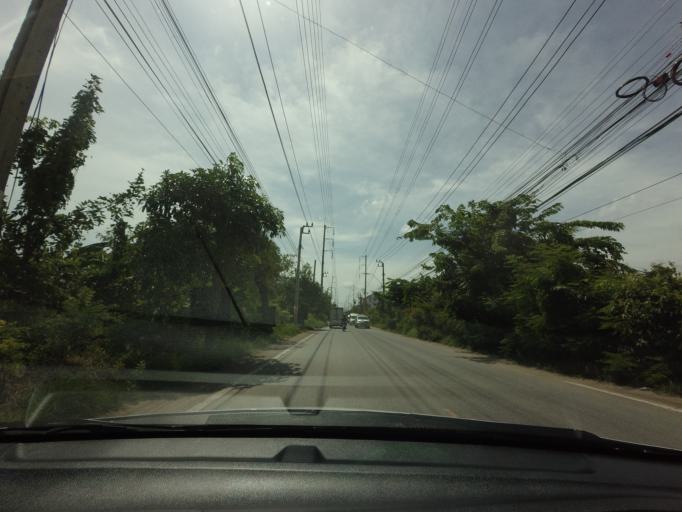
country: TH
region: Bangkok
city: Bang Na
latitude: 13.6189
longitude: 100.6593
